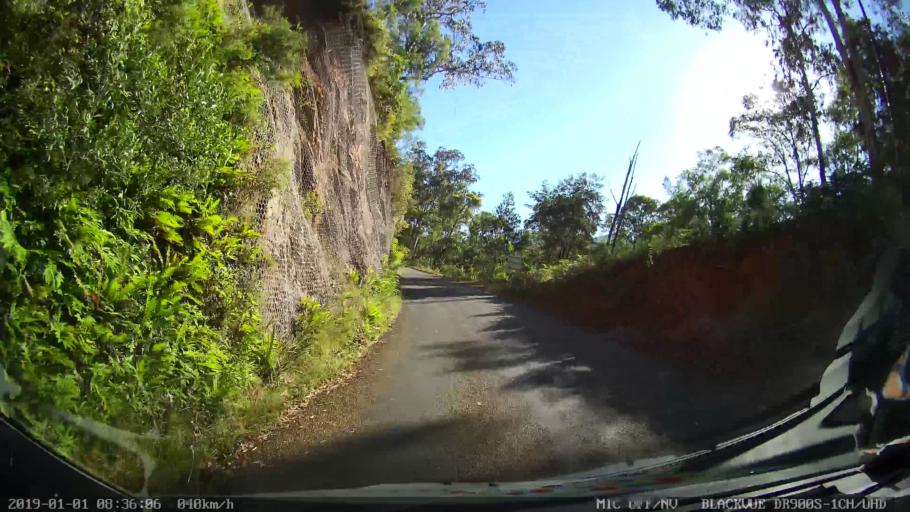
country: AU
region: New South Wales
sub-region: Snowy River
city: Jindabyne
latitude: -36.3457
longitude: 148.1941
